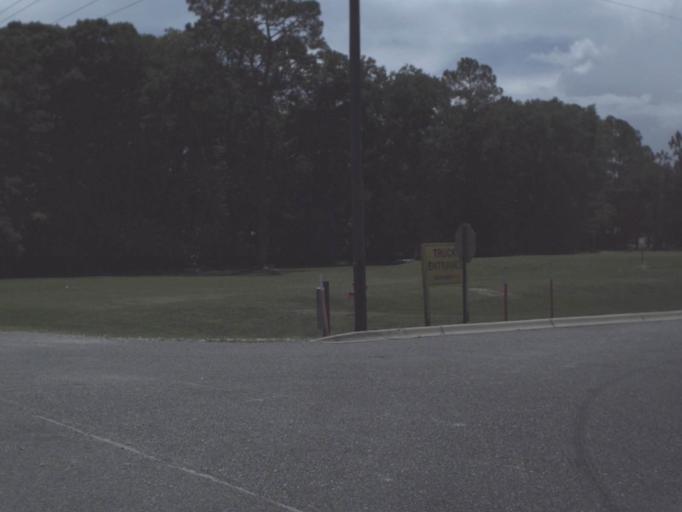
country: US
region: Florida
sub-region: Taylor County
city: Perry
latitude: 30.0861
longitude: -83.6566
